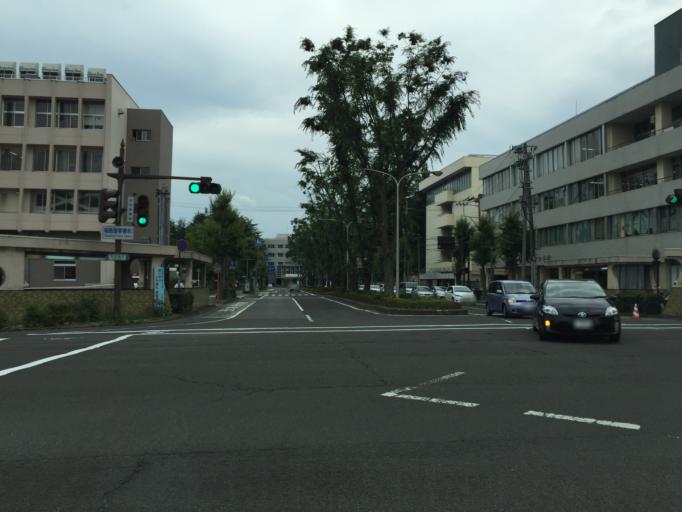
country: JP
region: Fukushima
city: Fukushima-shi
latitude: 37.7528
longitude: 140.4680
